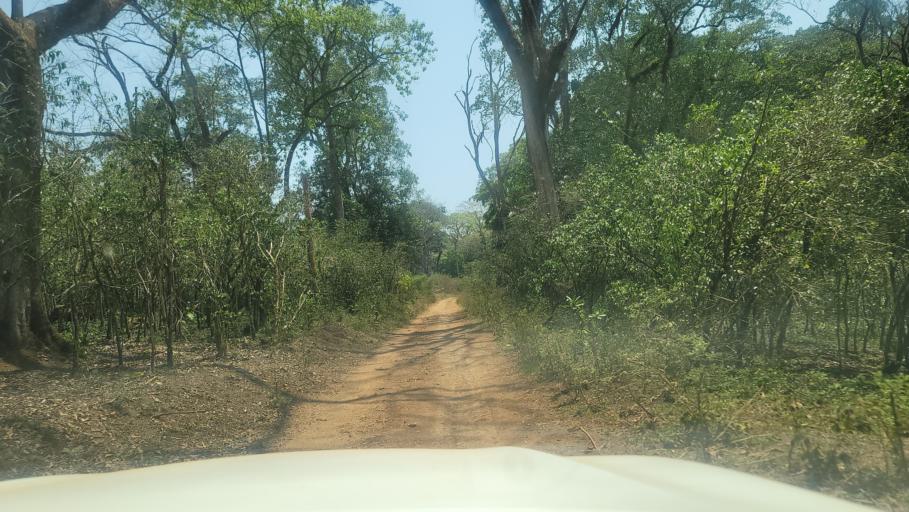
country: ET
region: Southern Nations, Nationalities, and People's Region
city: Bonga
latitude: 7.5094
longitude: 36.2228
